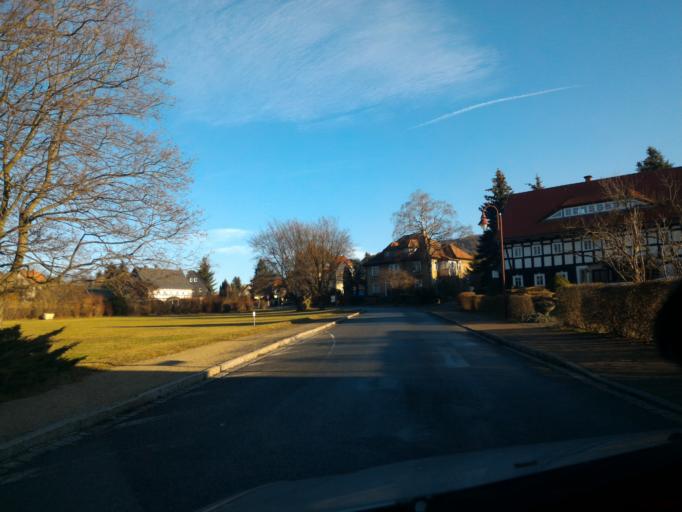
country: DE
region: Saxony
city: Kurort Jonsdorf
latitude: 50.8541
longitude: 14.6960
